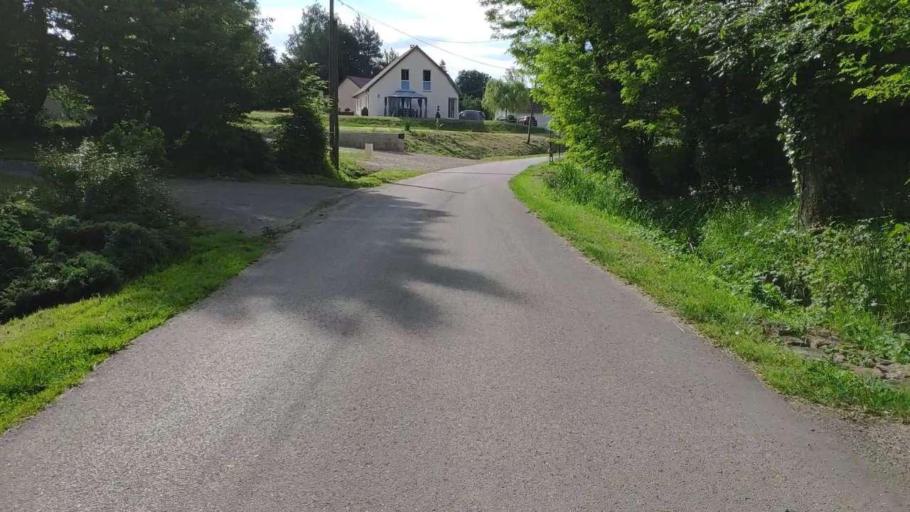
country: FR
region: Franche-Comte
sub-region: Departement du Jura
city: Bletterans
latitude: 46.7167
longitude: 5.4610
